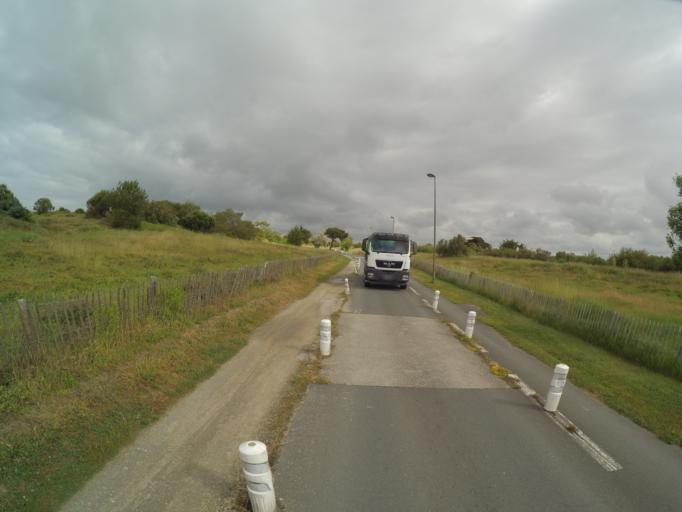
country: FR
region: Poitou-Charentes
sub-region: Departement de la Charente-Maritime
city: Aytre
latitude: 46.1206
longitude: -1.1238
